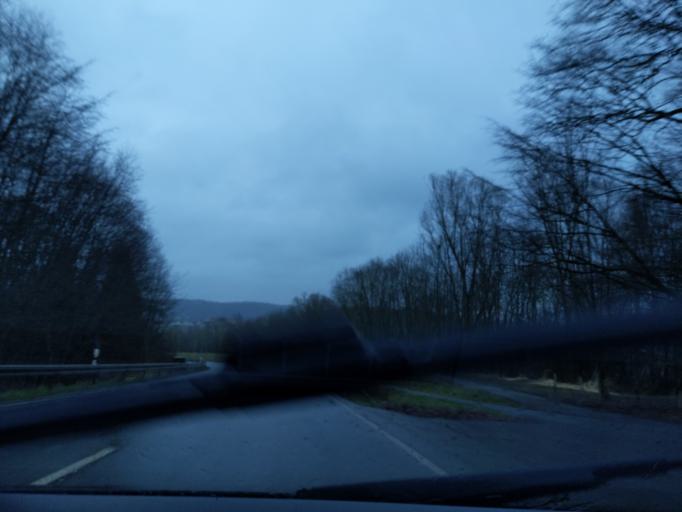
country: DE
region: Hesse
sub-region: Regierungsbezirk Kassel
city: Bad Arolsen
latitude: 51.3804
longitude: 9.0397
